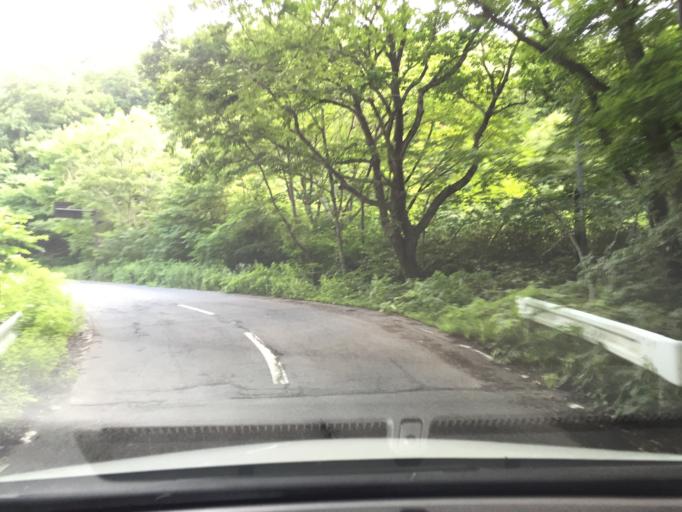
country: JP
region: Tochigi
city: Kuroiso
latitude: 37.2621
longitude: 140.0756
